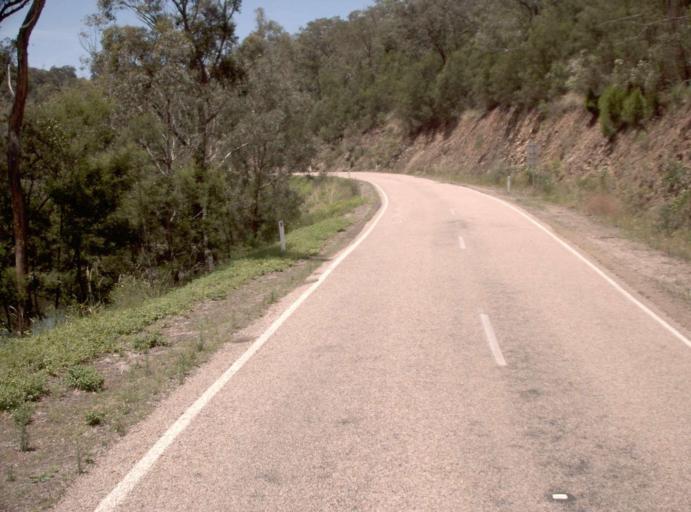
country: AU
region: Victoria
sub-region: East Gippsland
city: Lakes Entrance
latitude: -37.5272
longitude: 147.8503
